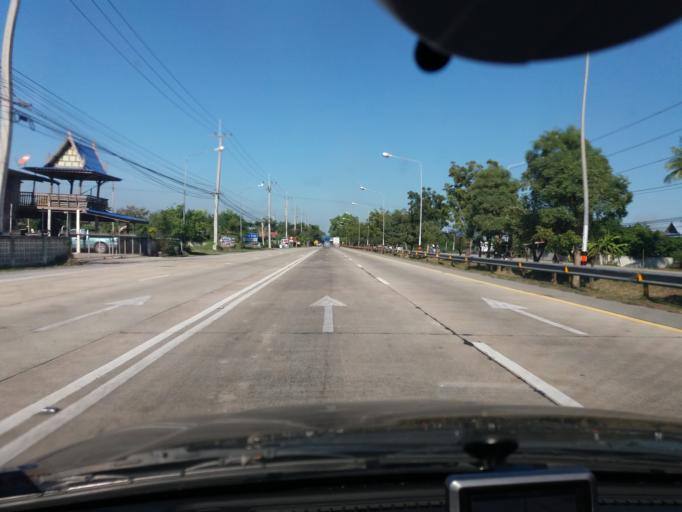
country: TH
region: Suphan Buri
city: Si Prachan
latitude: 14.5635
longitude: 100.1431
